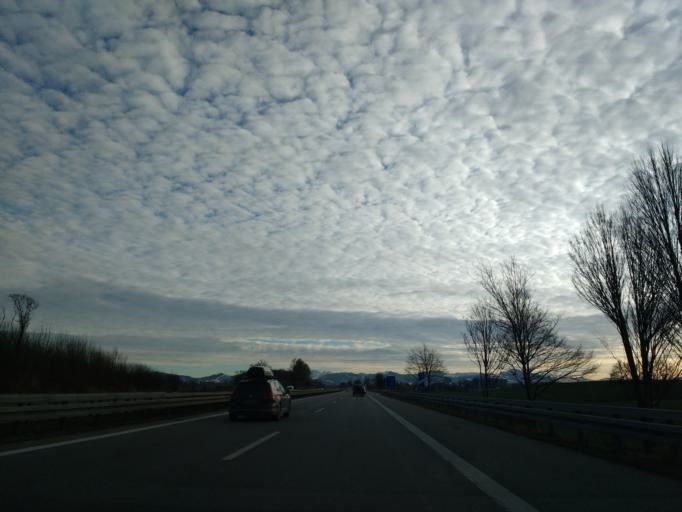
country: DE
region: Bavaria
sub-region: Swabia
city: Neuburg
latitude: 47.7594
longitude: 10.3278
